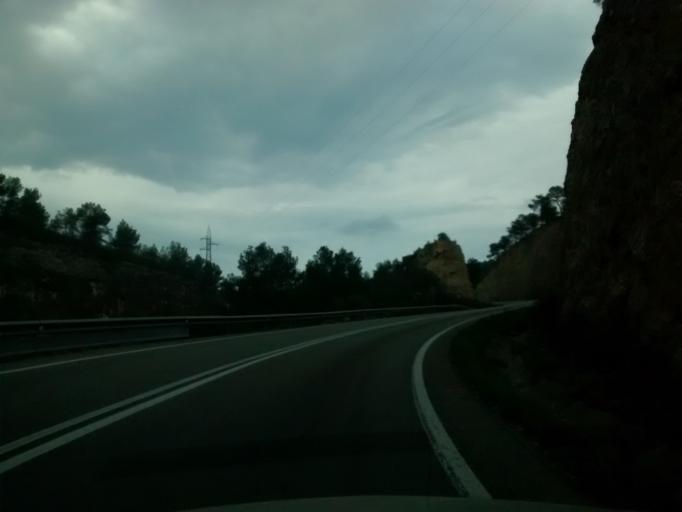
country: ES
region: Catalonia
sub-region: Provincia de Tarragona
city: Benifallet
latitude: 40.9887
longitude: 0.5131
